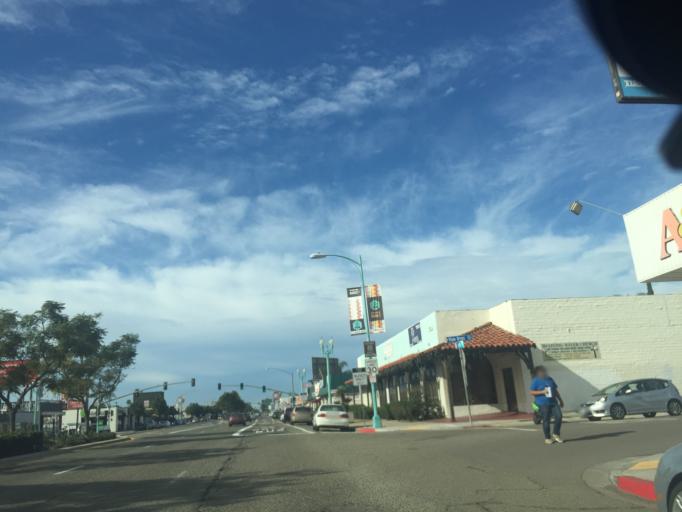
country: US
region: California
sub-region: San Diego County
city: San Diego
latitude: 32.7552
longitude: -117.1028
